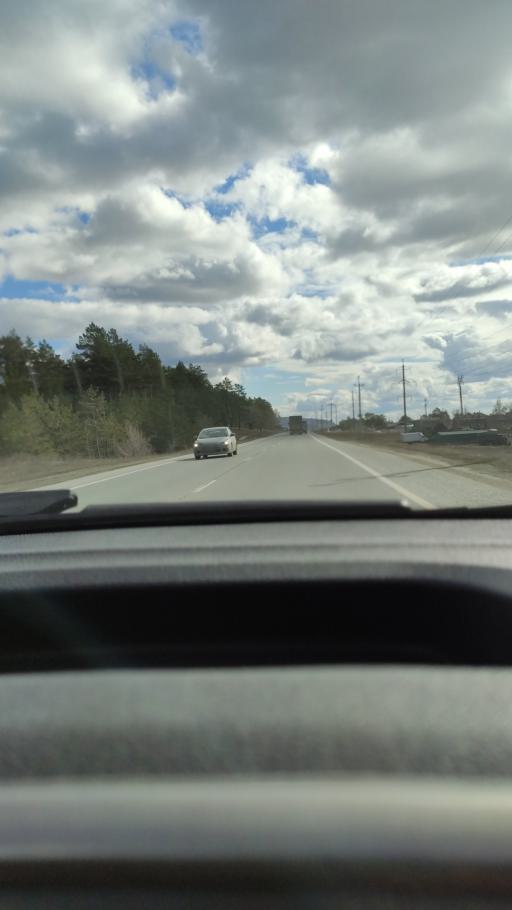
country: RU
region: Samara
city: Kurumoch
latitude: 53.4647
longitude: 50.0748
